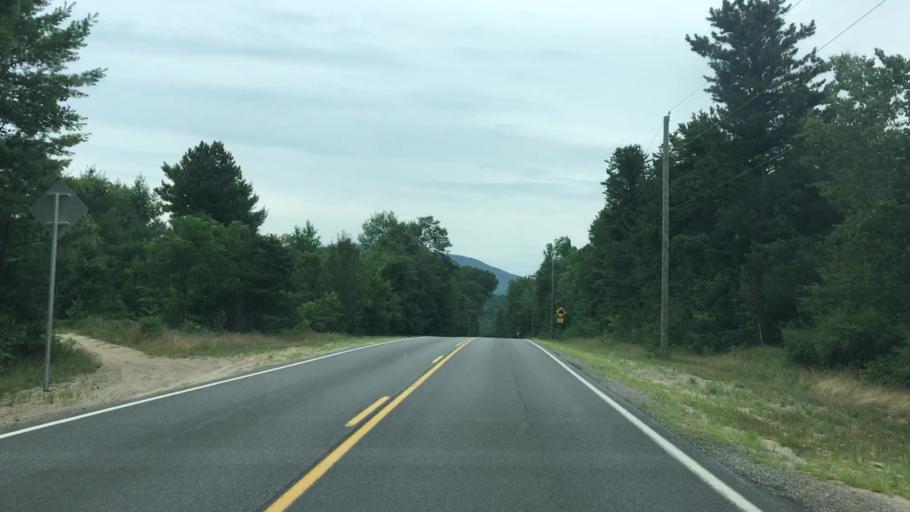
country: US
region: New York
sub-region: Essex County
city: Keeseville
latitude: 44.4697
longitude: -73.5921
